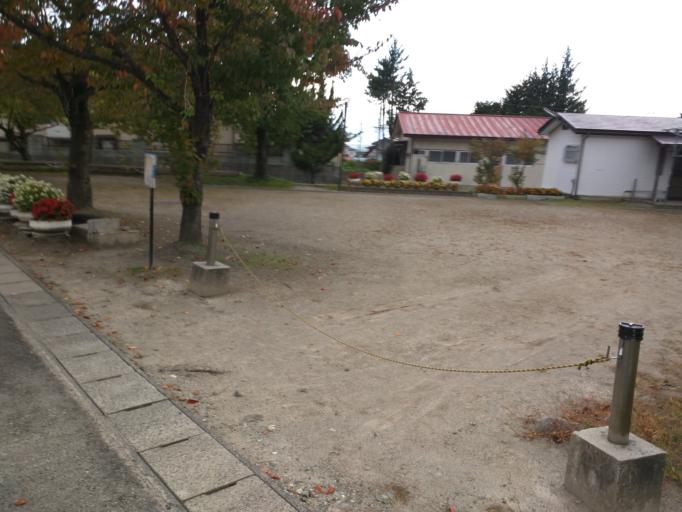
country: JP
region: Fukushima
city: Kitakata
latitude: 37.5176
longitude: 139.9521
